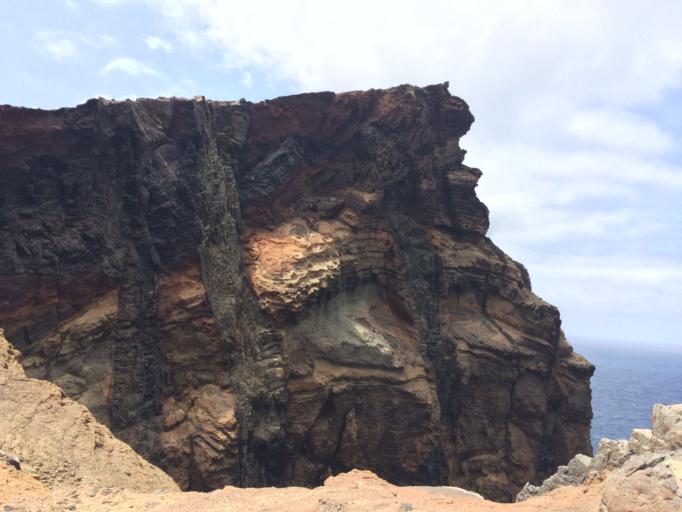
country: PT
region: Madeira
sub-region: Machico
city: Canical
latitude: 32.7506
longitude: -16.6945
